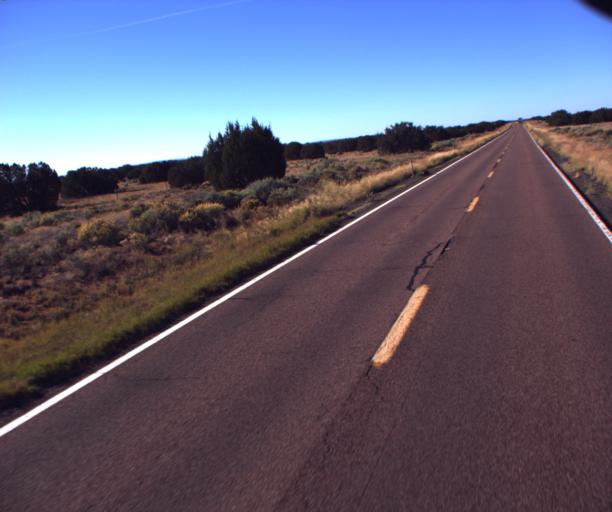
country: US
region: Arizona
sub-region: Navajo County
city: Heber-Overgaard
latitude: 34.5804
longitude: -110.4055
